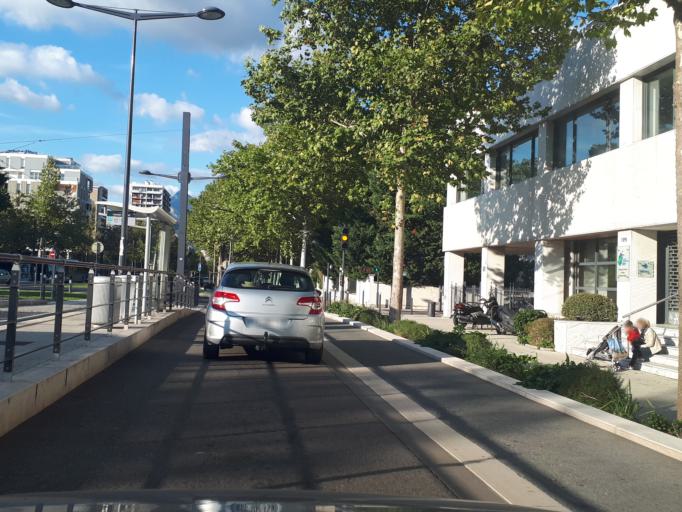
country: FR
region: Rhone-Alpes
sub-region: Departement de l'Isere
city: Grenoble
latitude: 45.1695
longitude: 5.7130
